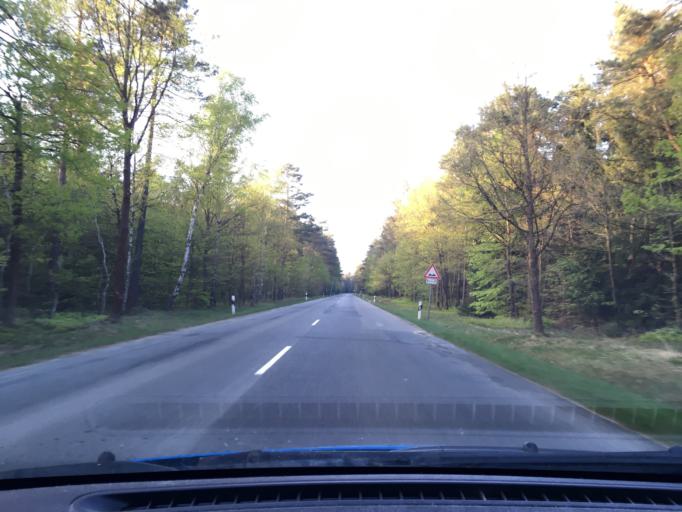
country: DE
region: Lower Saxony
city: Wietzendorf
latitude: 52.9886
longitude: 9.9919
